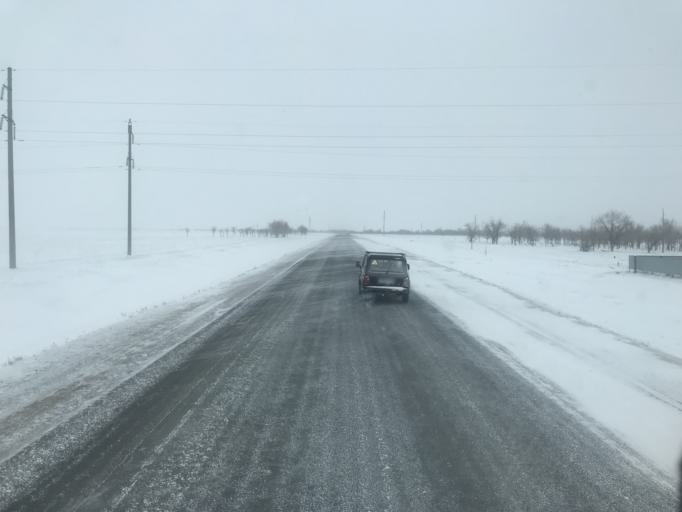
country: KZ
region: Batys Qazaqstan
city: Chapaev
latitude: 50.5172
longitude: 51.0599
